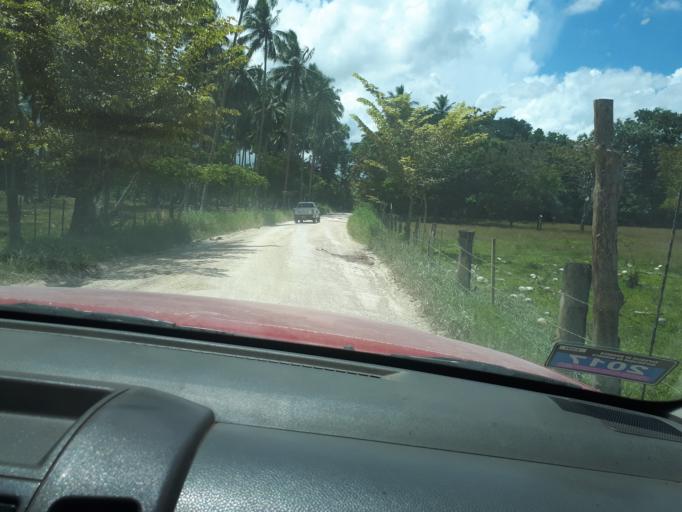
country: VU
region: Sanma
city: Luganville
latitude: -15.5860
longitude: 167.0490
